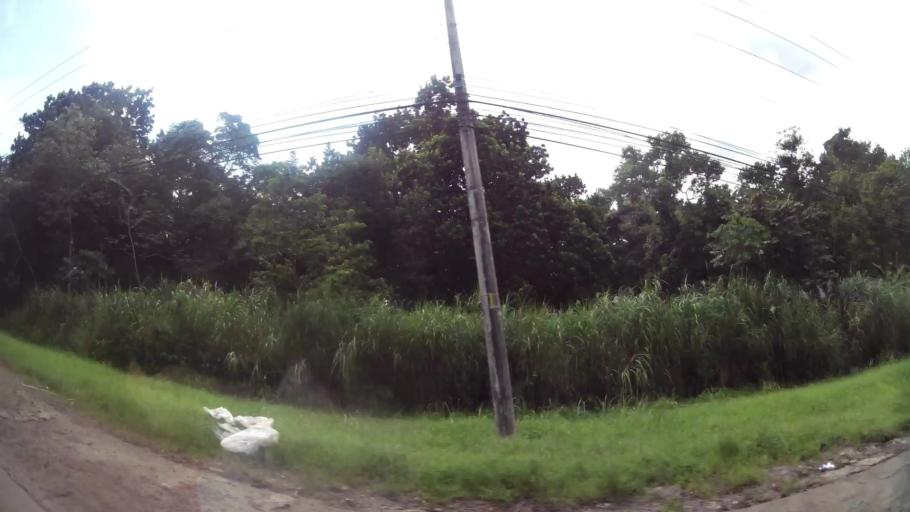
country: PA
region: Panama
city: Panama
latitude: 9.0368
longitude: -79.5425
